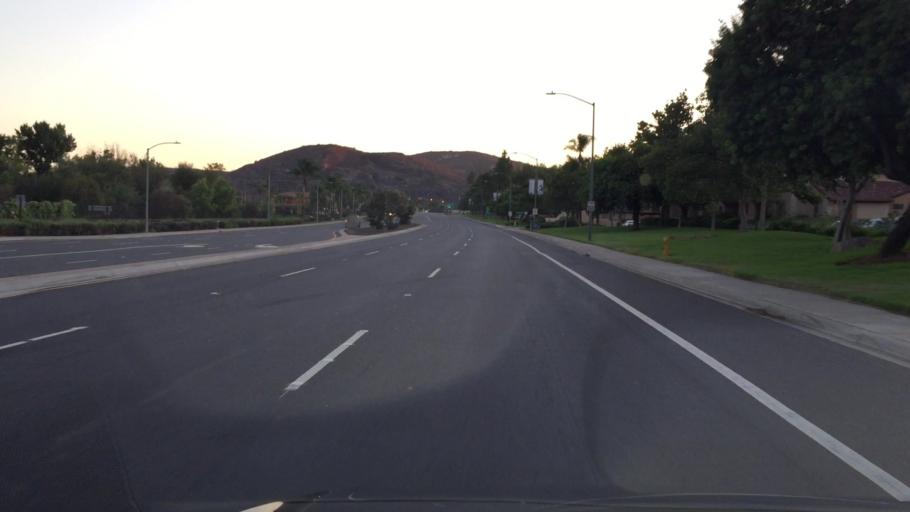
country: US
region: California
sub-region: San Diego County
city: Rancho San Diego
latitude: 32.7428
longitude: -116.9351
